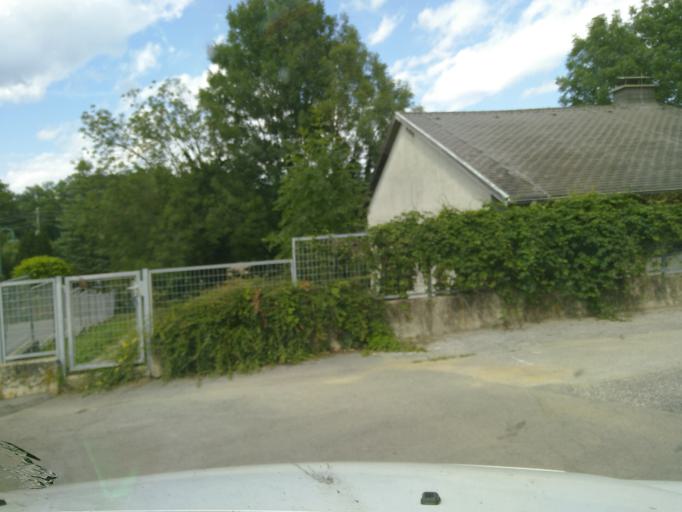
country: AT
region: Burgenland
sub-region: Politischer Bezirk Oberpullendorf
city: Nikitsch
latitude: 47.5297
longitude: 16.6465
